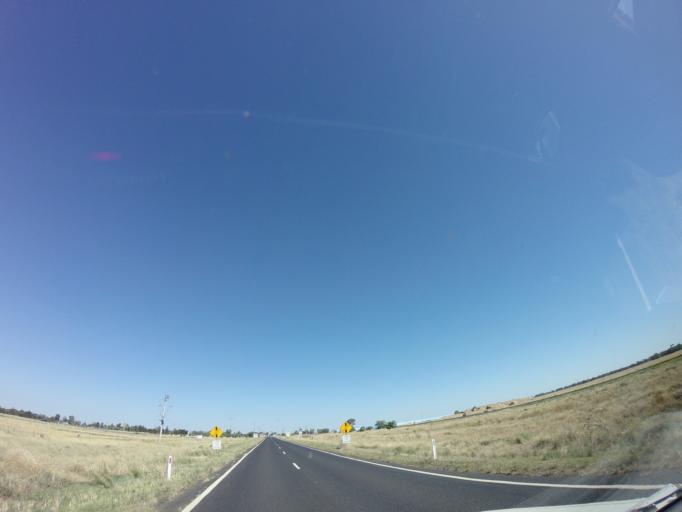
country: AU
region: New South Wales
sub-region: Bogan
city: Nyngan
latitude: -31.8336
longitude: 147.7098
